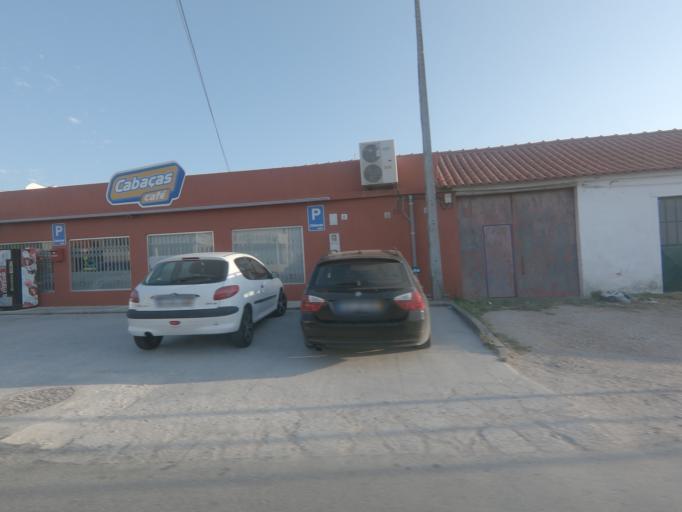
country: PT
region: Santarem
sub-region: Alcanena
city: Alcanena
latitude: 39.4833
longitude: -8.6323
